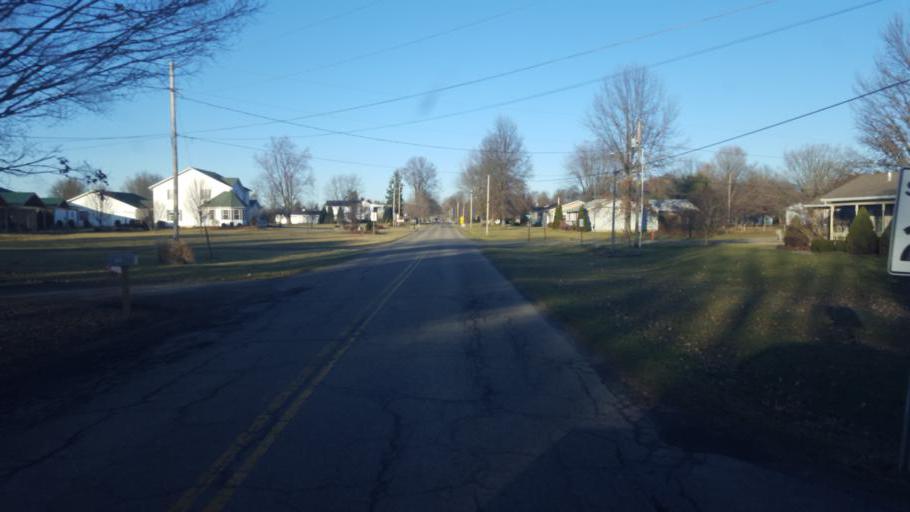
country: US
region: Ohio
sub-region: Knox County
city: Fredericktown
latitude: 40.4709
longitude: -82.5507
